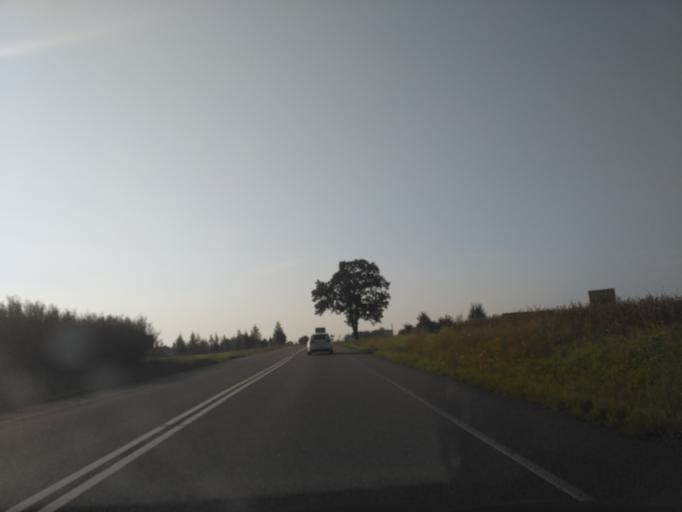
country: PL
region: Lublin Voivodeship
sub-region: Powiat janowski
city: Modliborzyce
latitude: 50.7419
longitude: 22.3459
